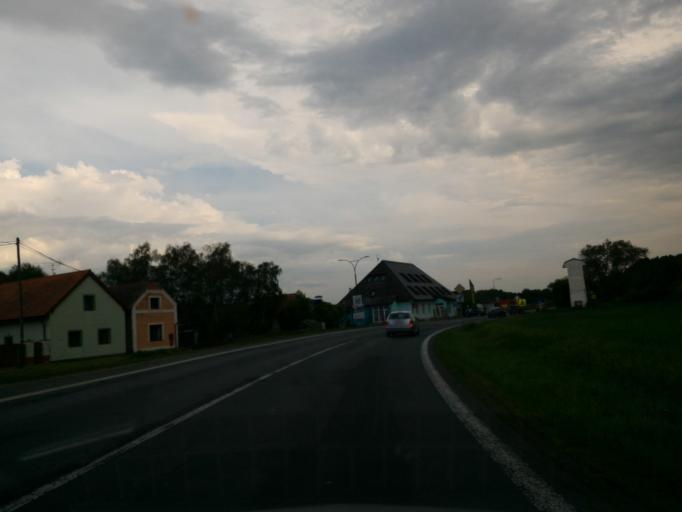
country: CZ
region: Central Bohemia
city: Velky Osek
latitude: 50.1020
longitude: 15.1459
